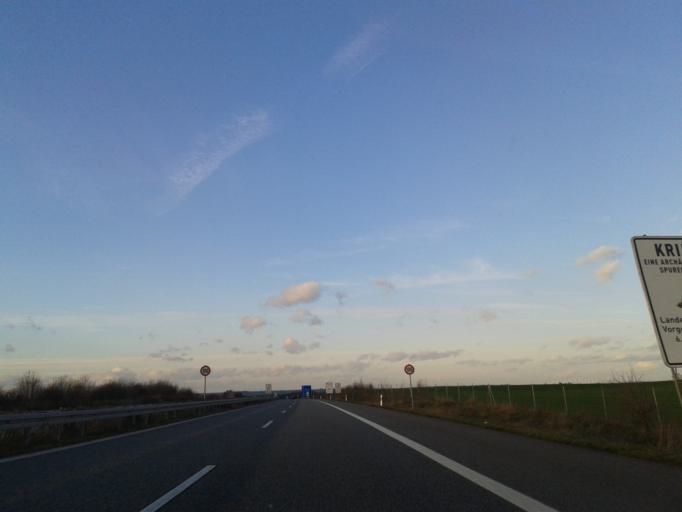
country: DE
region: Saxony-Anhalt
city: Zscherben
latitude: 51.4731
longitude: 11.8527
